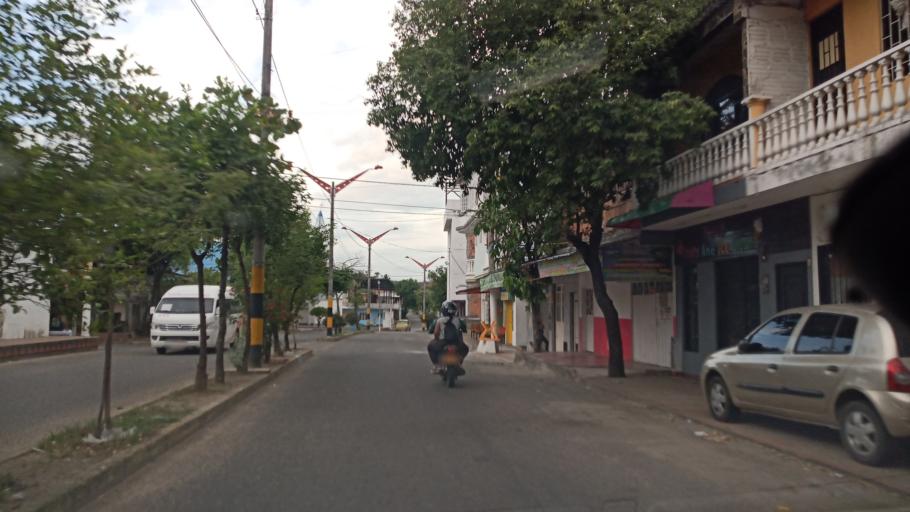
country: CO
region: Tolima
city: Melgar
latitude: 4.2008
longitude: -74.6491
